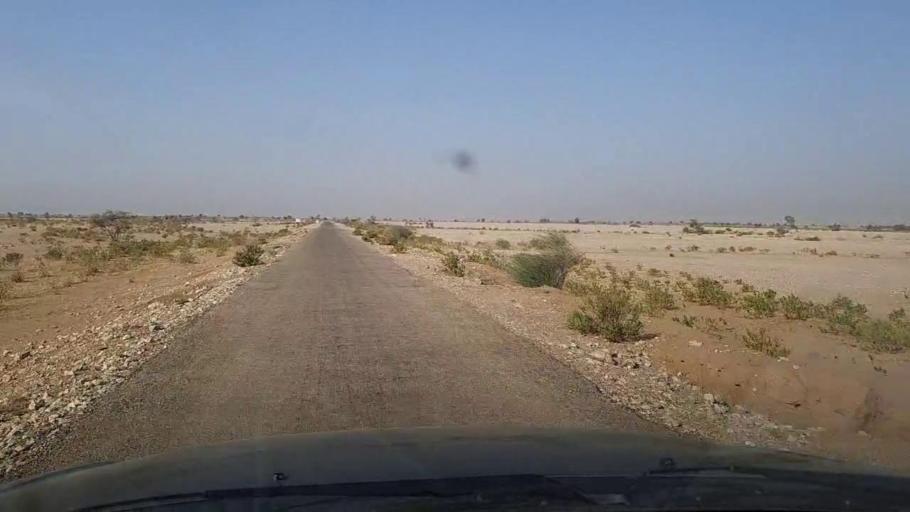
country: PK
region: Sindh
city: Sann
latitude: 25.9869
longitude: 68.0656
